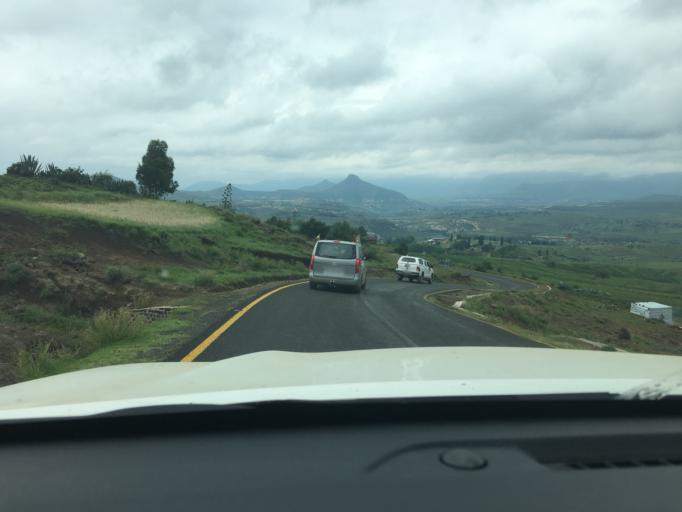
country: LS
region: Berea
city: Teyateyaneng
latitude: -29.2563
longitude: 27.8417
